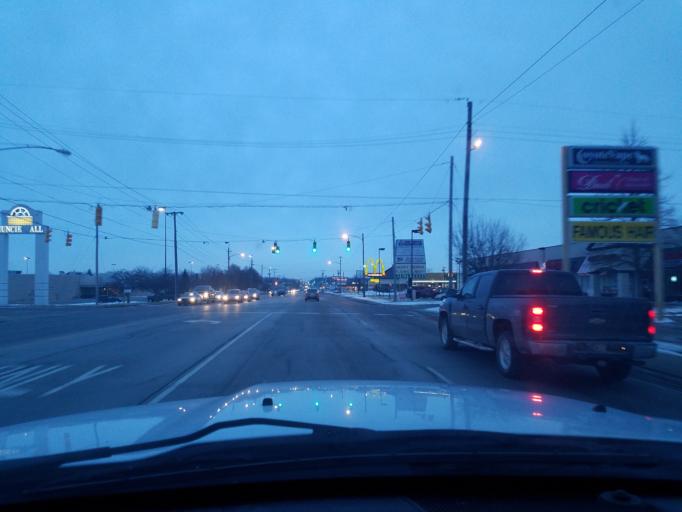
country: US
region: Indiana
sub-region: Delaware County
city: Muncie
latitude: 40.2190
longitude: -85.3779
